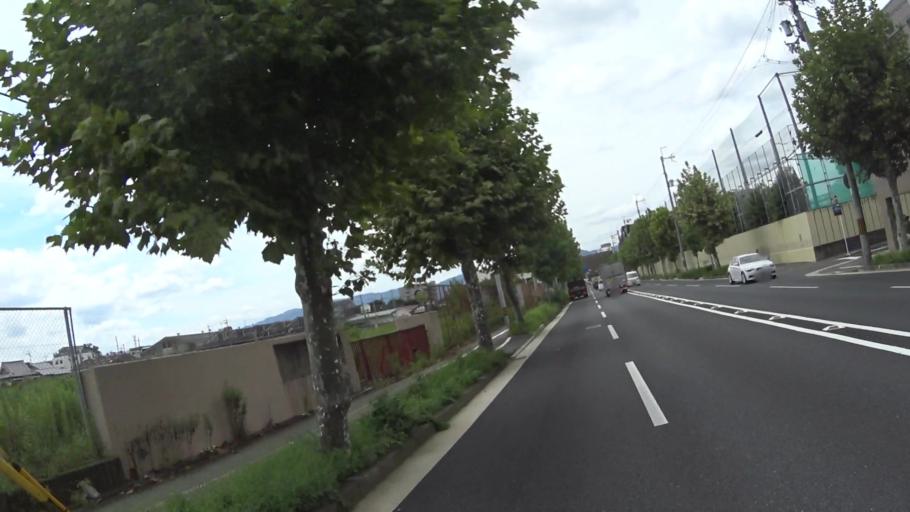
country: JP
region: Kyoto
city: Muko
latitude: 34.9734
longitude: 135.7398
